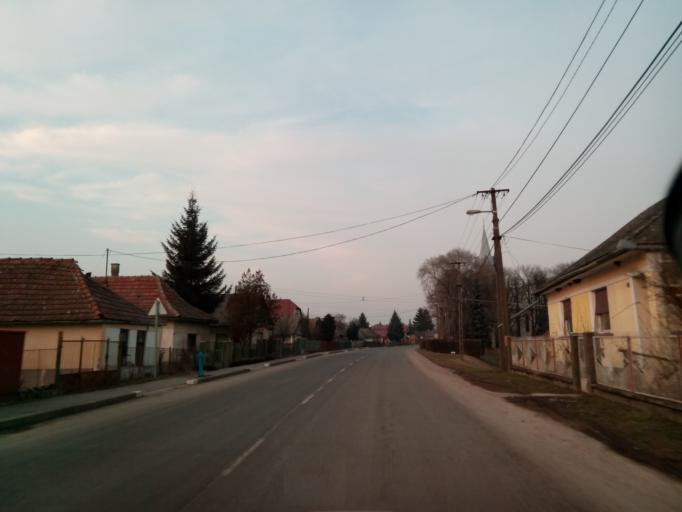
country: HU
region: Borsod-Abauj-Zemplen
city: Gonc
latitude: 48.5196
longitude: 21.2501
